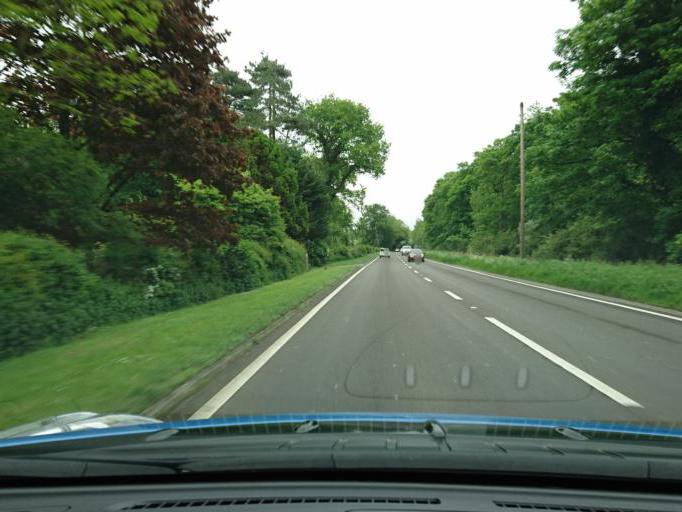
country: GB
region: England
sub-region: Oxfordshire
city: Stanford in the Vale
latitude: 51.6784
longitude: -1.4882
